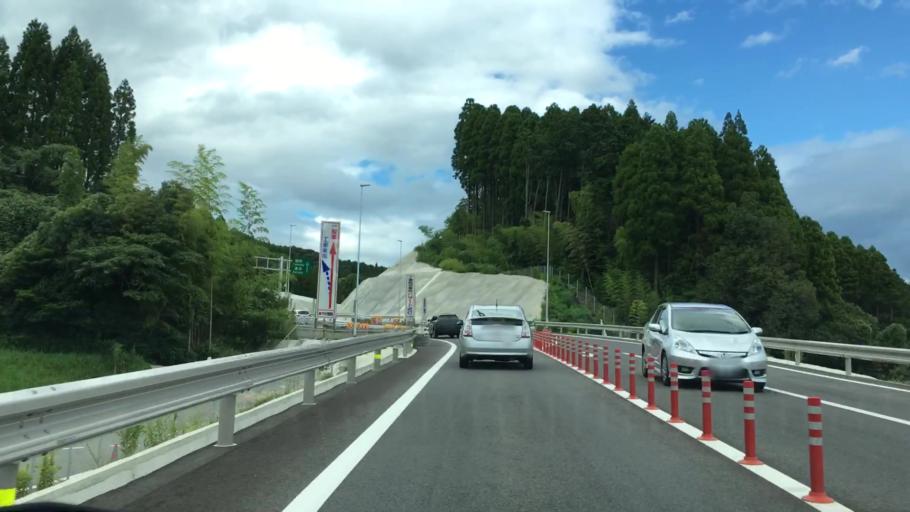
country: JP
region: Saga Prefecture
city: Imaricho-ko
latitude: 33.2953
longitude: 129.9125
